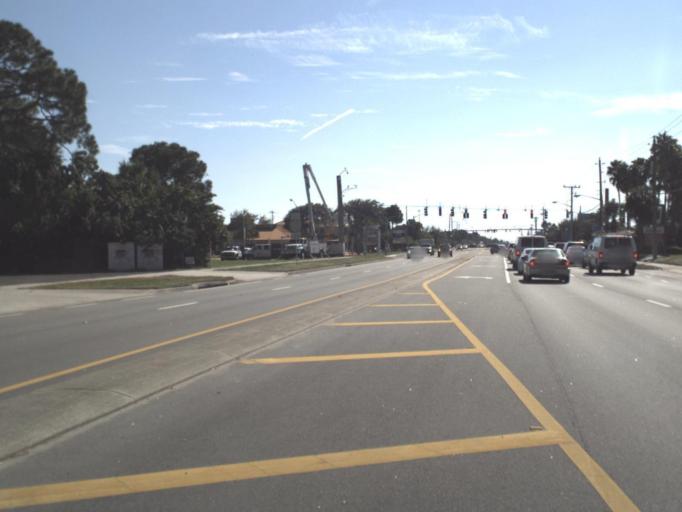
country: US
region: Florida
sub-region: Brevard County
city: South Patrick Shores
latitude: 28.2046
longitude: -80.6721
